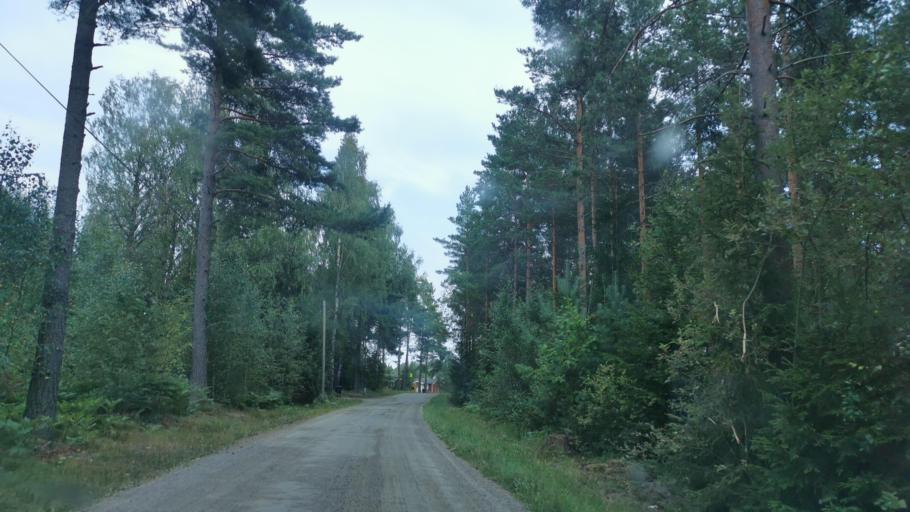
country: SE
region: OEstergoetland
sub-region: Norrkopings Kommun
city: Svartinge
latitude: 58.7252
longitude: 15.9476
